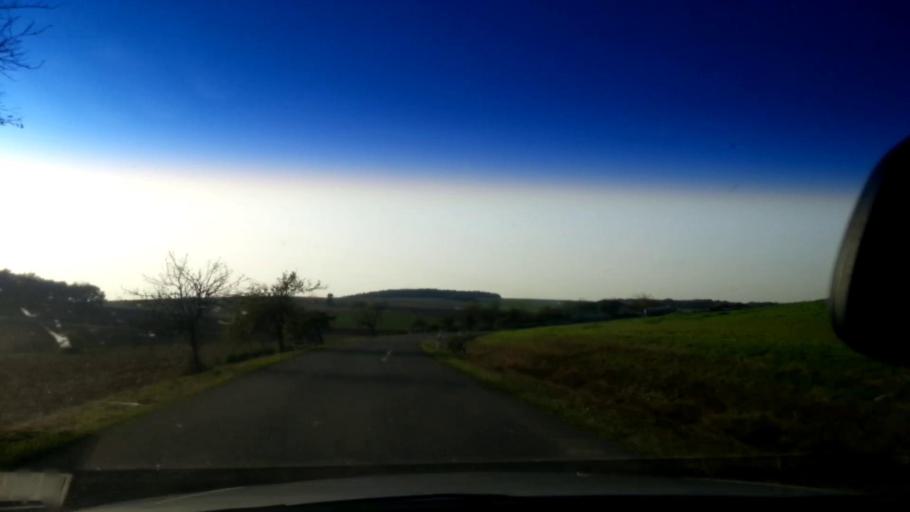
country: DE
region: Bavaria
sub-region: Upper Franconia
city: Ebensfeld
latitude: 50.0276
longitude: 10.9805
